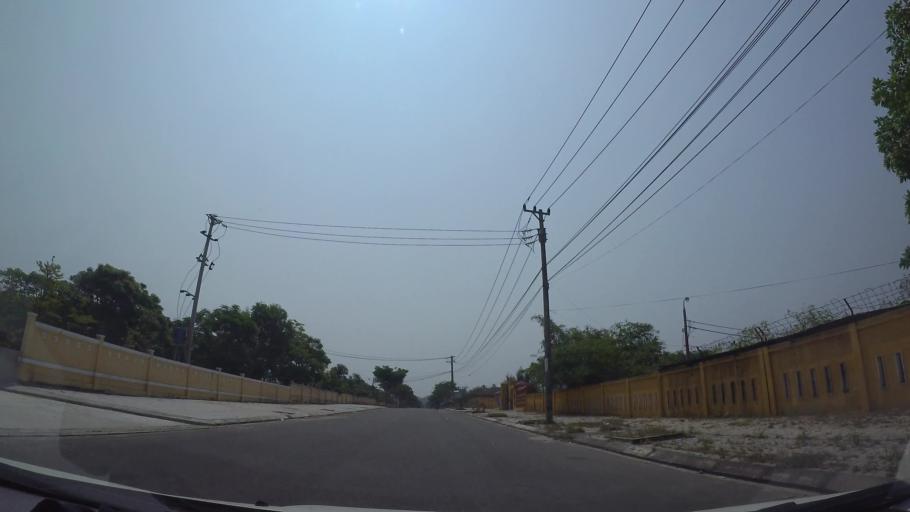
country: VN
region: Da Nang
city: Ngu Hanh Son
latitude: 16.0175
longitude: 108.2506
